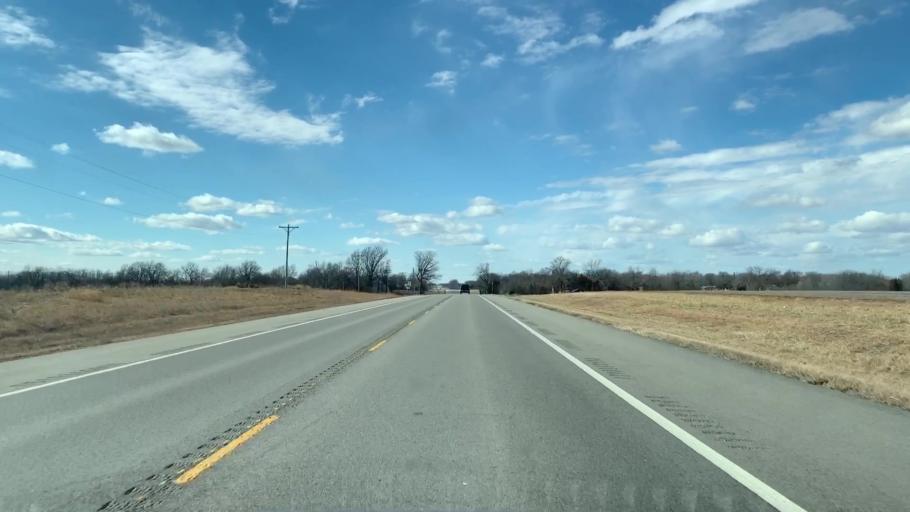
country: US
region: Kansas
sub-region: Labette County
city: Oswego
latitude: 37.3402
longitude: -95.0815
